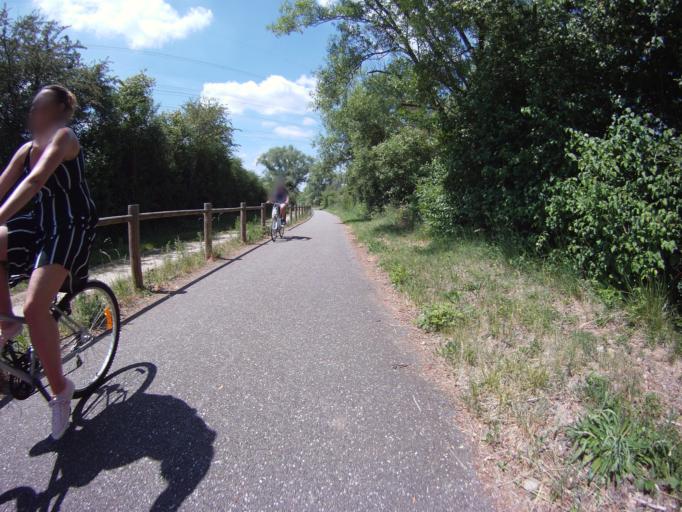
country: FR
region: Lorraine
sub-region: Departement de Meurthe-et-Moselle
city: Eulmont
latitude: 48.7409
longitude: 6.2477
